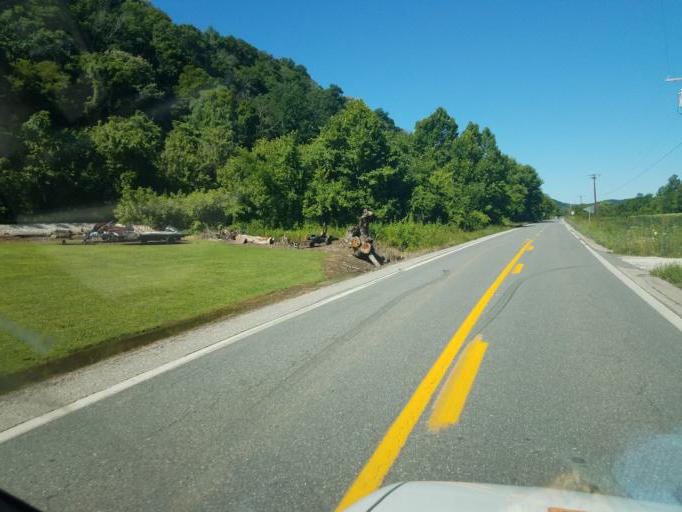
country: US
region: West Virginia
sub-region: Cabell County
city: Lesage
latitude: 38.5907
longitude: -82.1899
